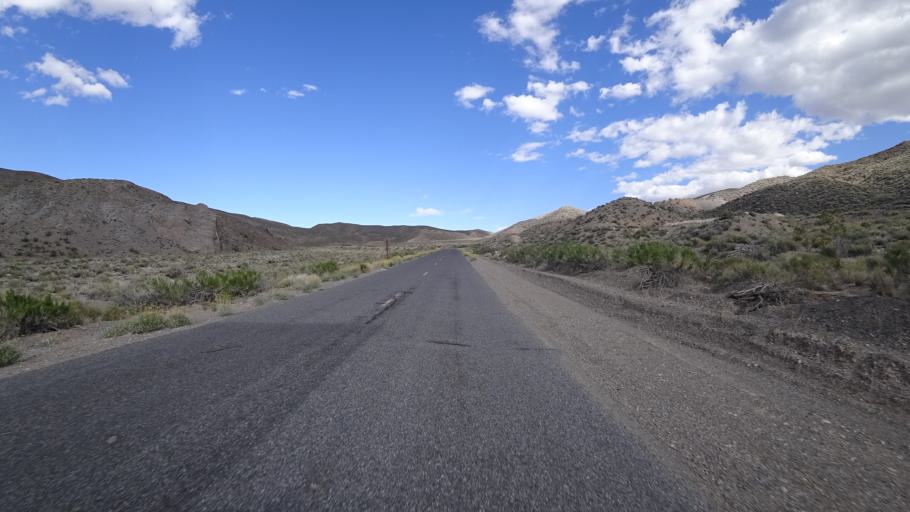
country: US
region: Nevada
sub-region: Nye County
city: Beatty
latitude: 36.4148
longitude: -117.1838
